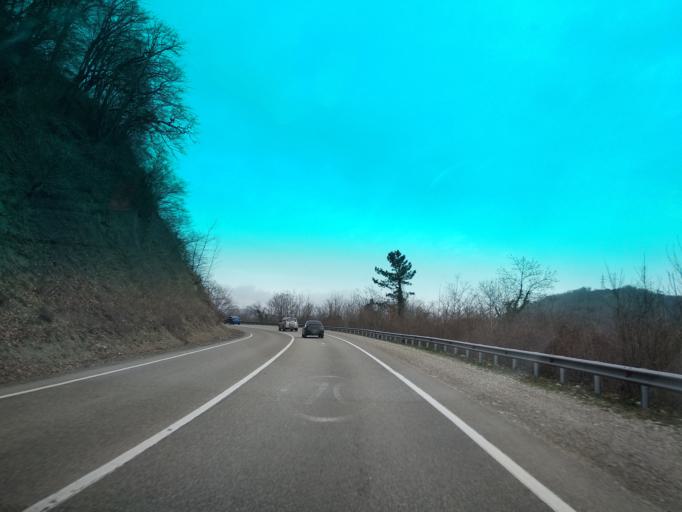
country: RU
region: Krasnodarskiy
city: Ol'ginka
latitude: 44.2214
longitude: 38.8951
